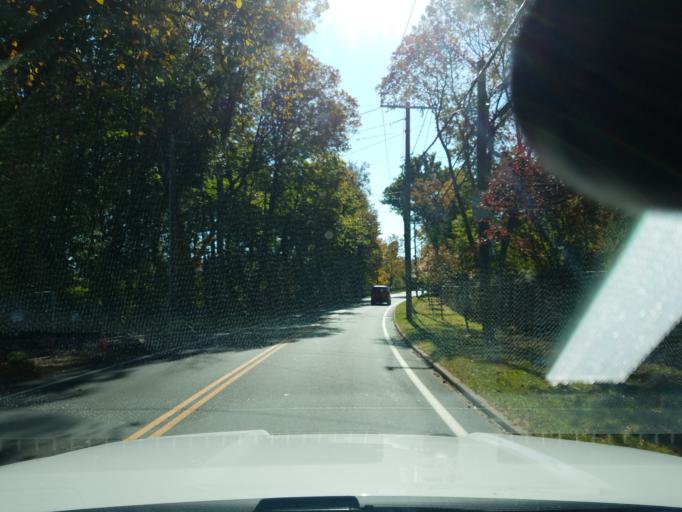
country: US
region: Connecticut
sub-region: Fairfield County
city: Glenville
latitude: 41.0873
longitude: -73.6283
